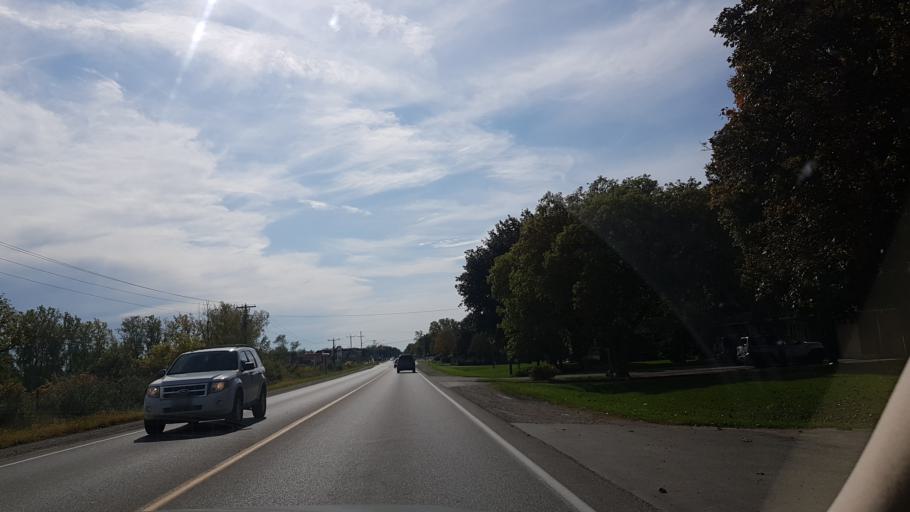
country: CA
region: Ontario
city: Delaware
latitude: 42.9469
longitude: -81.4286
